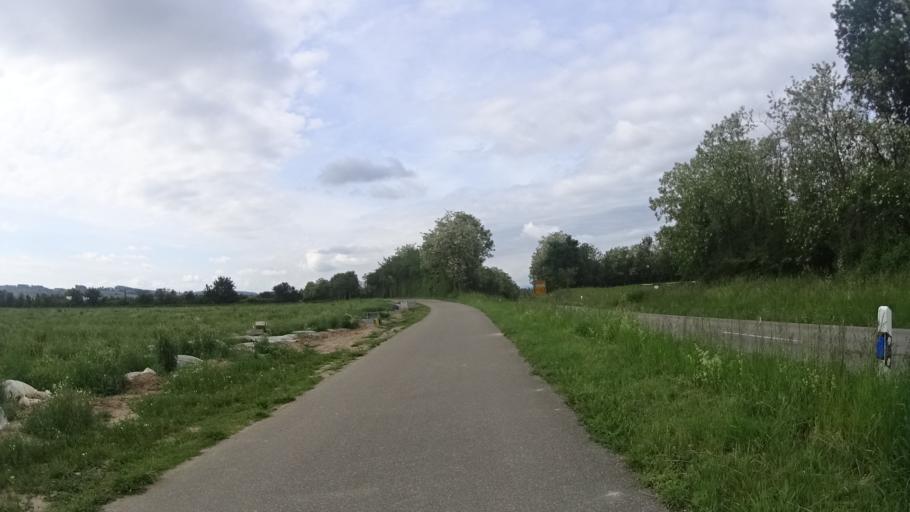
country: DE
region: Baden-Wuerttemberg
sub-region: Freiburg Region
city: Schliengen
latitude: 47.7773
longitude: 7.5532
